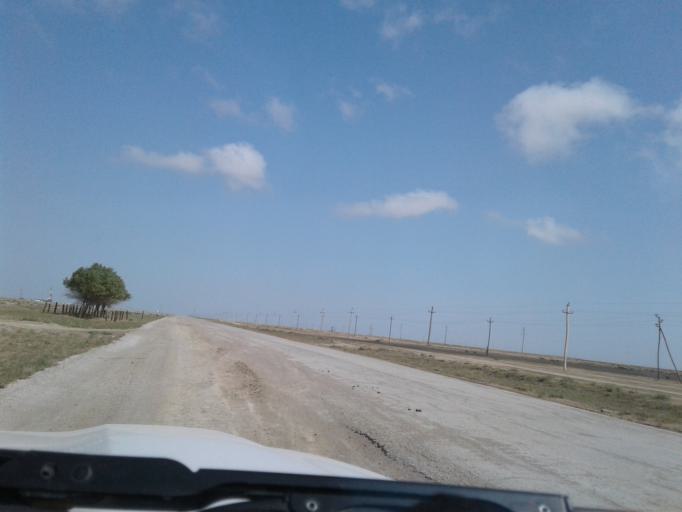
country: IR
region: Golestan
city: Gomishan
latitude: 37.7302
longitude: 53.9371
